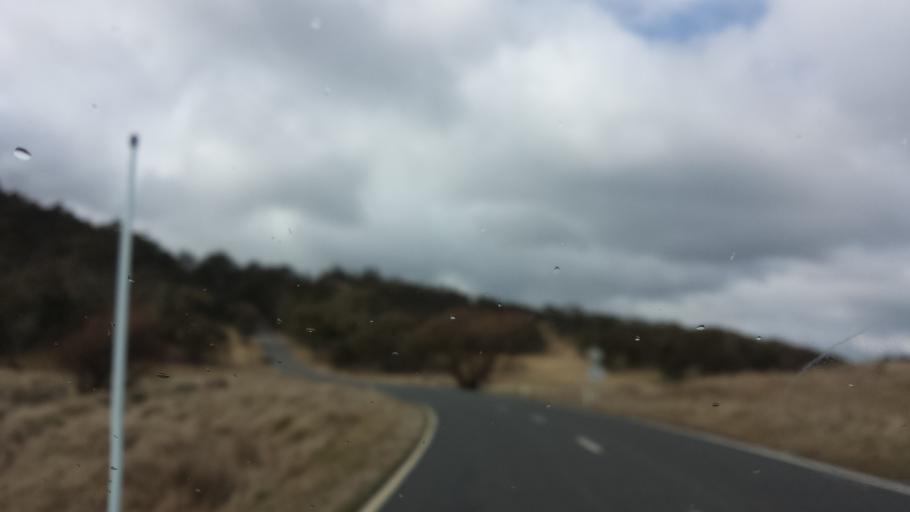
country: AU
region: Victoria
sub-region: Alpine
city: Mount Beauty
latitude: -37.1349
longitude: 147.4856
